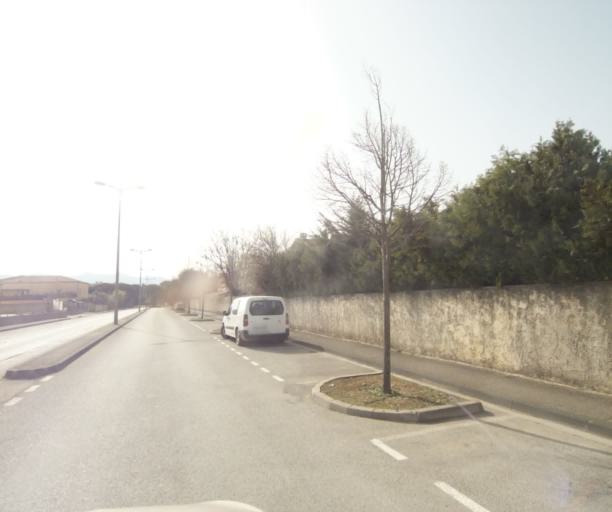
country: FR
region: Provence-Alpes-Cote d'Azur
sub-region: Departement des Bouches-du-Rhone
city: Gardanne
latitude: 43.4584
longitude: 5.4786
